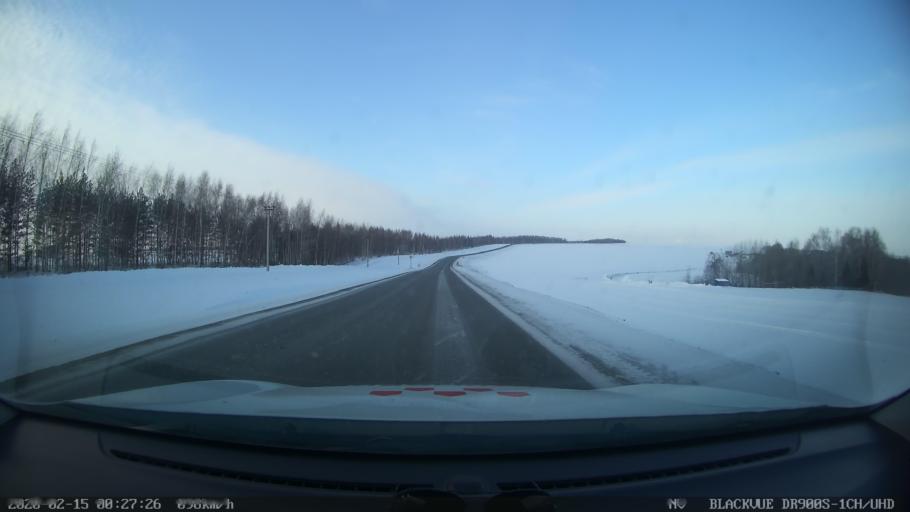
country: RU
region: Tatarstan
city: Verkhniy Uslon
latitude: 55.6281
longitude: 48.8744
